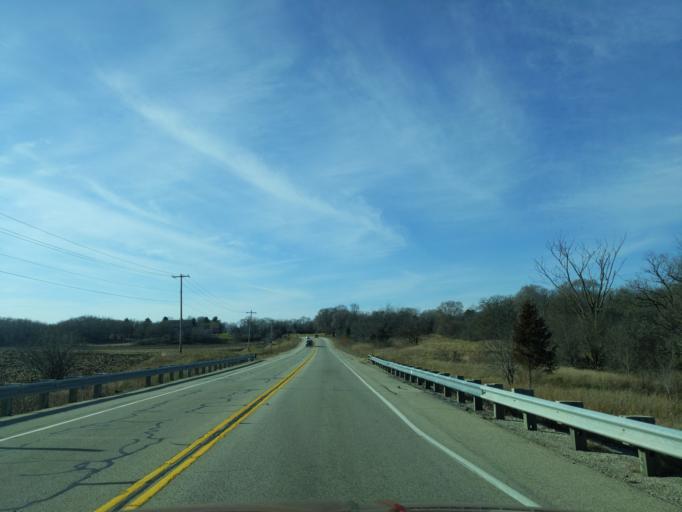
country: US
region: Wisconsin
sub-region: Jefferson County
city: Palmyra
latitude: 42.7994
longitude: -88.6038
